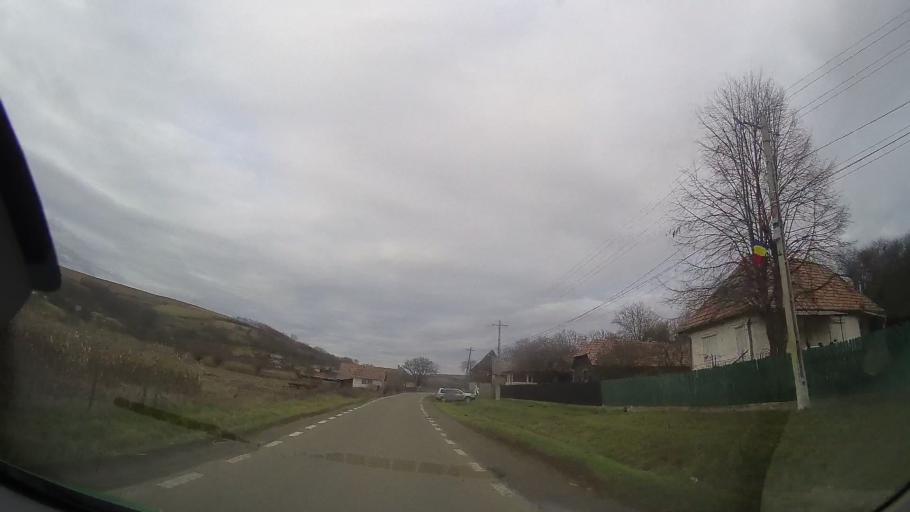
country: RO
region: Mures
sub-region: Comuna Cozma
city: Cozma
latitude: 46.8041
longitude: 24.5288
